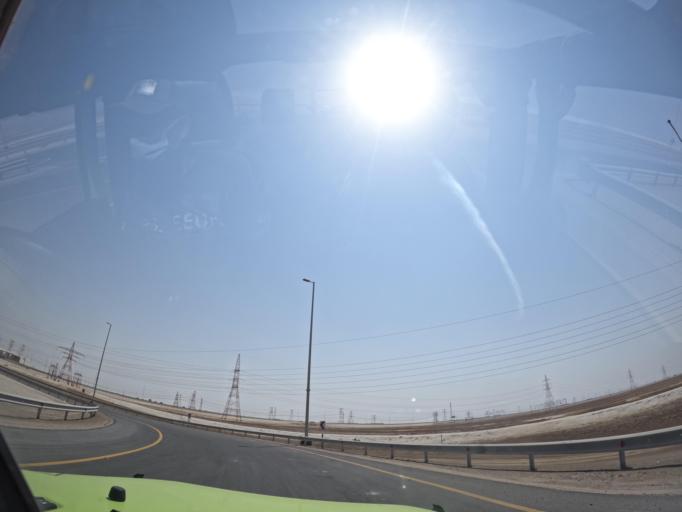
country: AE
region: Abu Dhabi
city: Abu Dhabi
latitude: 24.1659
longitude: 54.3505
